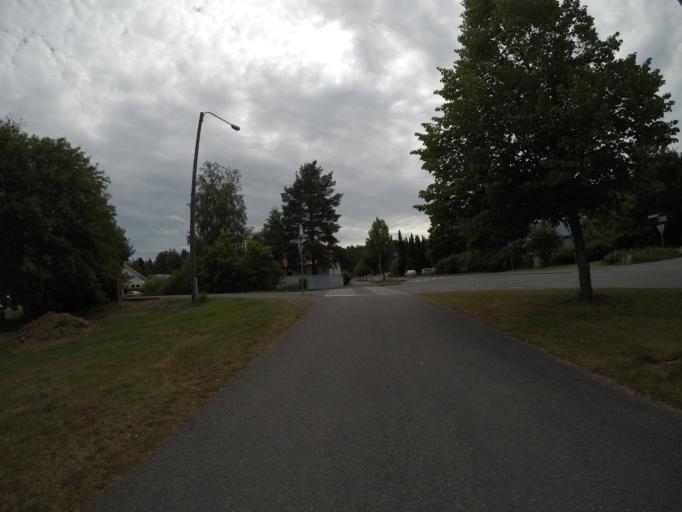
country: FI
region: Haeme
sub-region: Haemeenlinna
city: Parola
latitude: 61.0099
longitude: 24.3981
